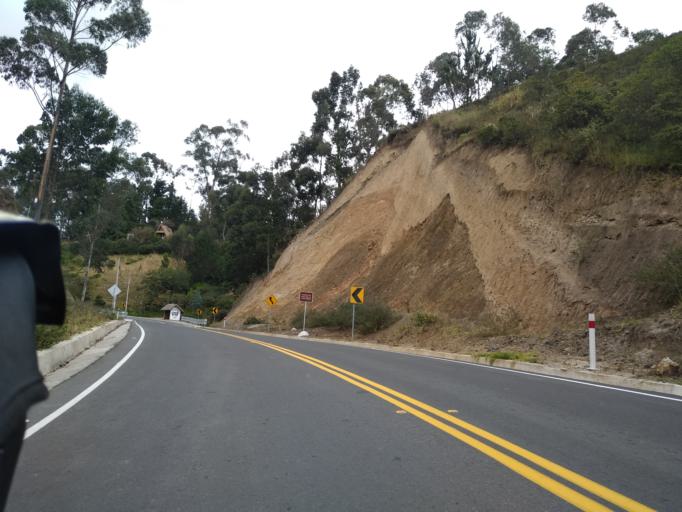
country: EC
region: Cotopaxi
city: Saquisili
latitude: -0.7964
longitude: -78.9157
